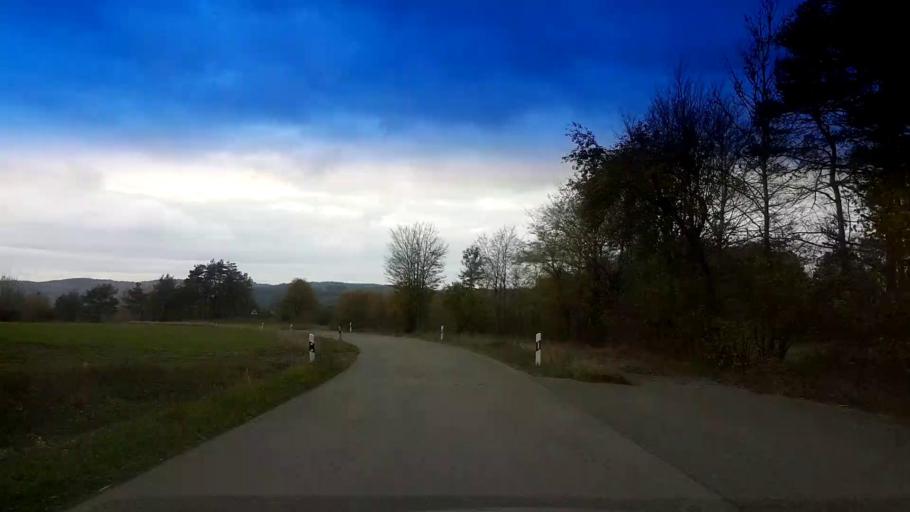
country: DE
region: Bavaria
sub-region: Upper Franconia
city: Wattendorf
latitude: 50.0203
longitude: 11.1113
